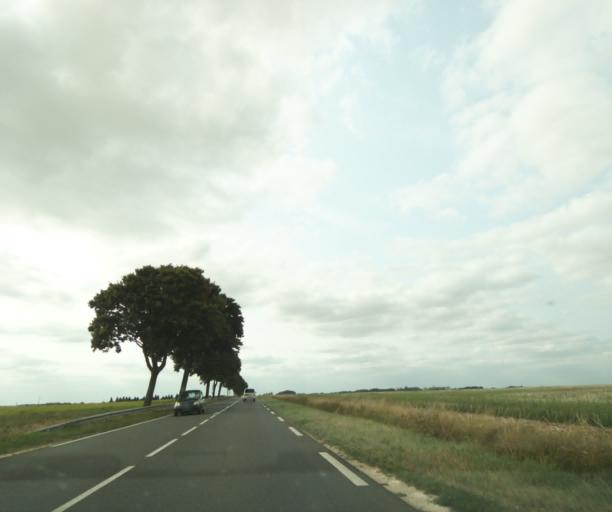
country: FR
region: Centre
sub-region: Departement d'Indre-et-Loire
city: Reignac-sur-Indre
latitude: 47.2009
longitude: 0.9127
